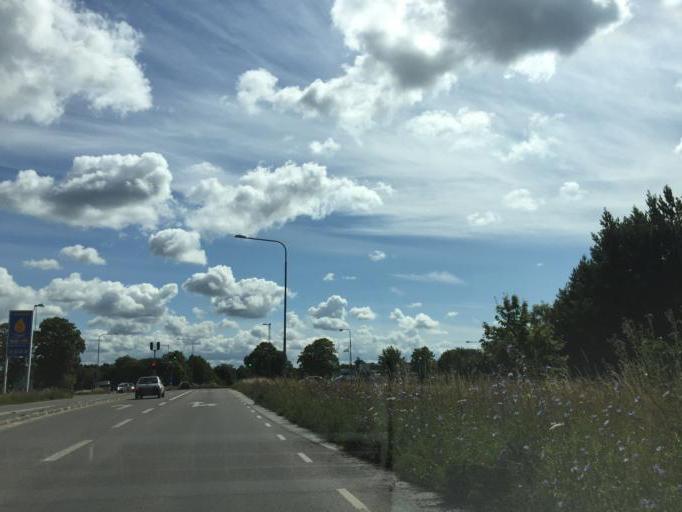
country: SE
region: Gotland
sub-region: Gotland
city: Visby
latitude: 57.6175
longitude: 18.2835
